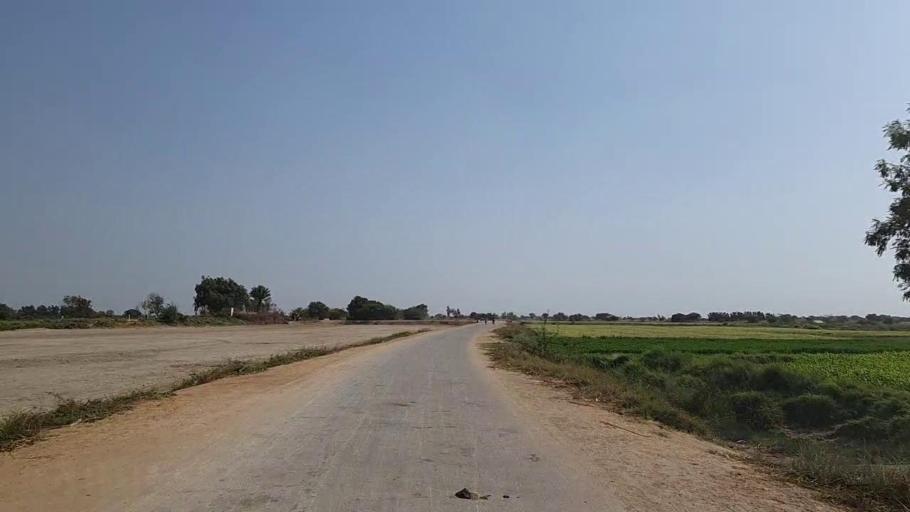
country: PK
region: Sindh
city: Daro Mehar
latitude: 24.7893
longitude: 68.1792
